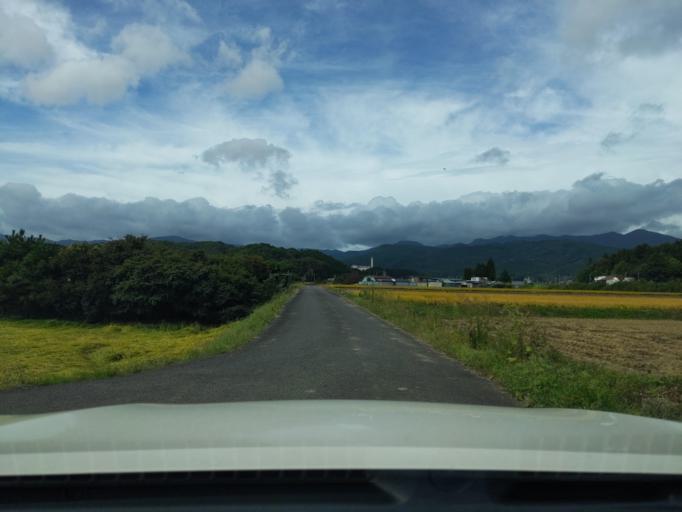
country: JP
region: Fukushima
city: Koriyama
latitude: 37.4132
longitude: 140.2868
